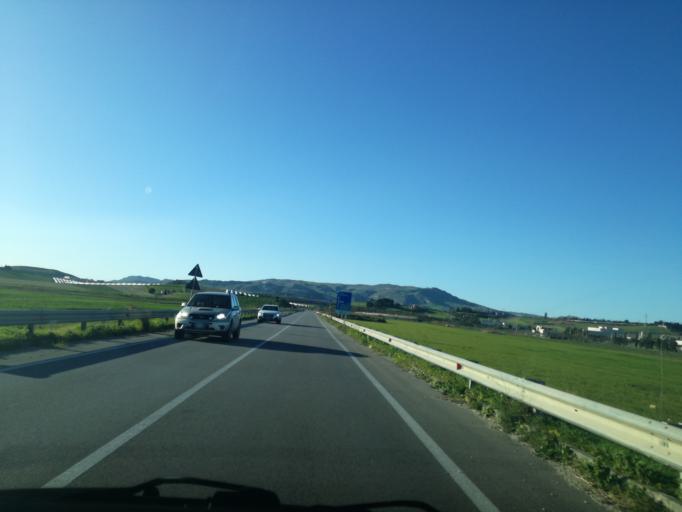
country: IT
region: Sicily
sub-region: Provincia di Caltanissetta
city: Butera
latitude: 37.1243
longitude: 14.1239
